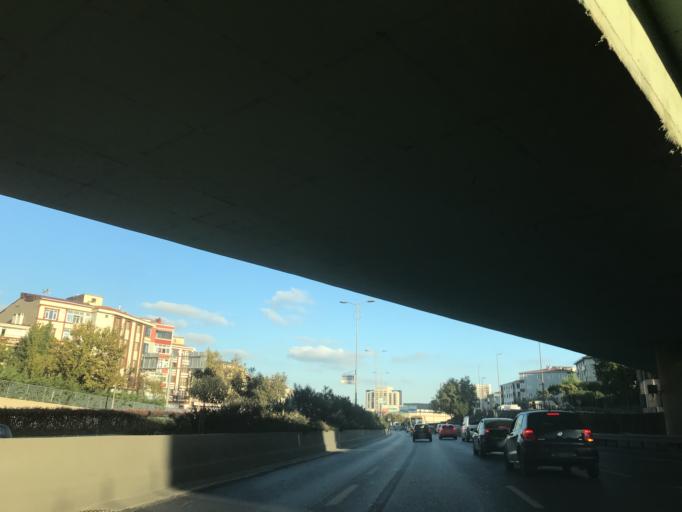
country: TR
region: Istanbul
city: Esenler
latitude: 41.0477
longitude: 28.8771
